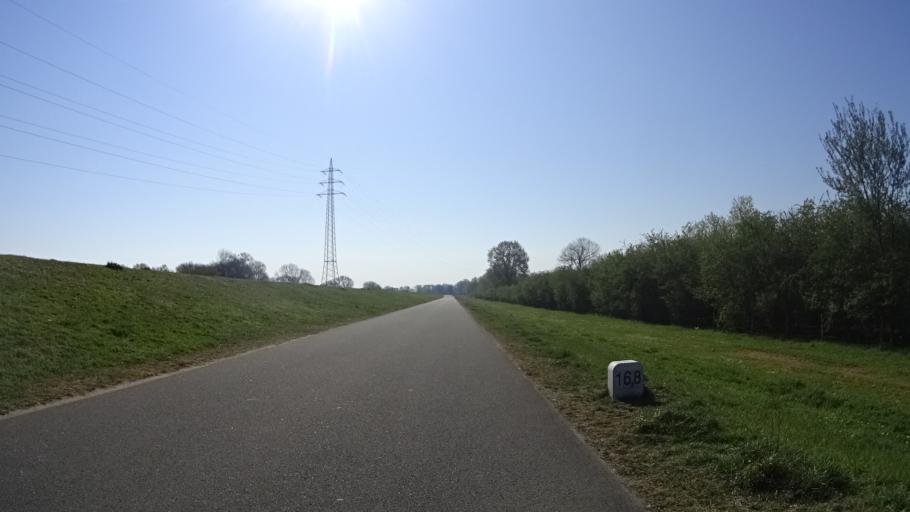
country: DE
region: North Rhine-Westphalia
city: Rheinberg
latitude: 51.5745
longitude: 6.5852
